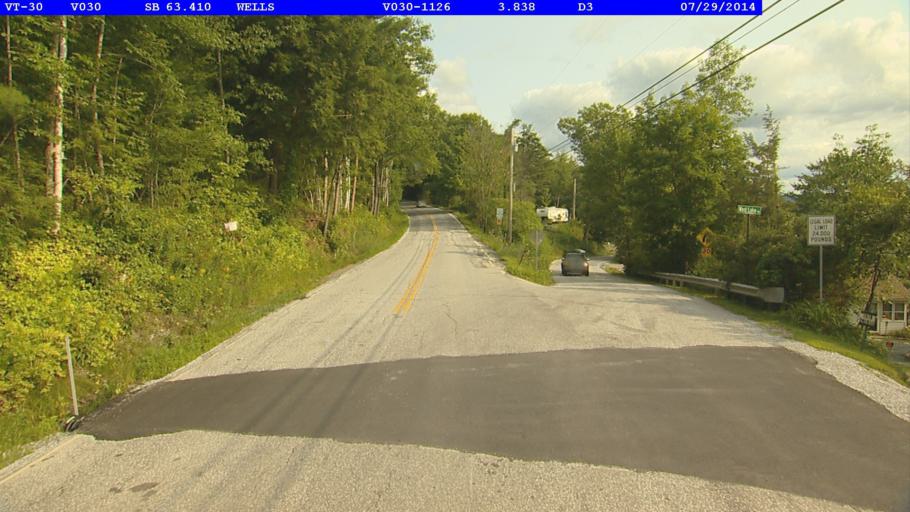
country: US
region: New York
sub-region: Washington County
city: Granville
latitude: 43.4463
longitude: -73.2031
